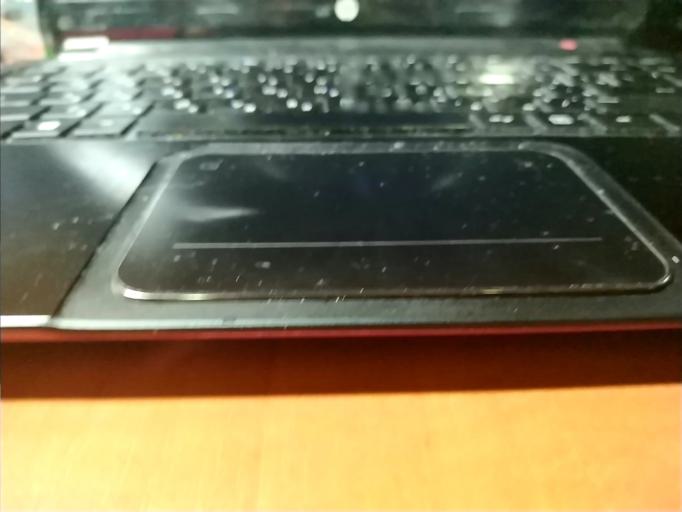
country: RU
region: Tverskaya
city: Ves'yegonsk
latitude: 58.6976
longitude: 37.5439
